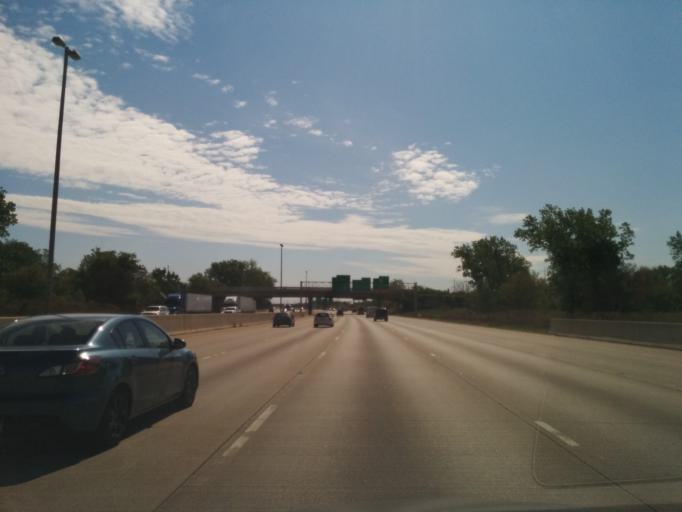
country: US
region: Indiana
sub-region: Lake County
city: Gary
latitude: 41.5678
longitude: -87.3489
